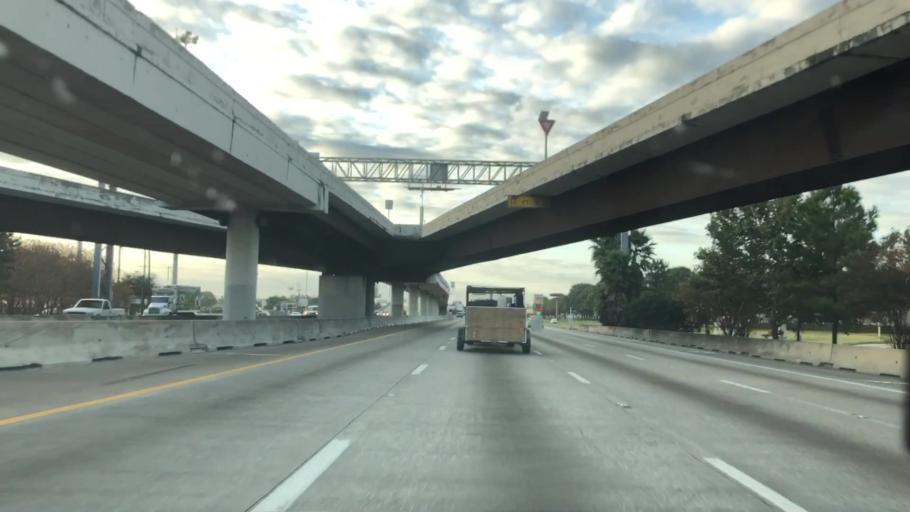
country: US
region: Texas
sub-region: Harris County
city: Aldine
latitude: 29.9199
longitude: -95.4126
